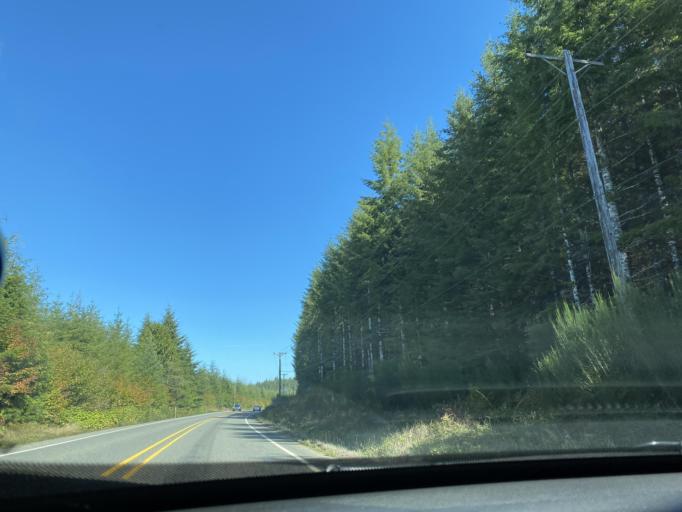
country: US
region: Washington
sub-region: Clallam County
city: Forks
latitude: 47.9598
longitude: -124.4464
